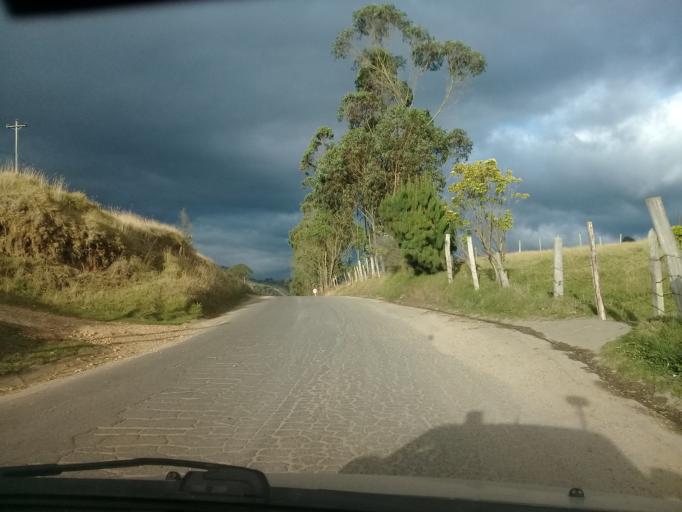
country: CO
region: Cundinamarca
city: Villapinzon
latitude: 5.2147
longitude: -73.6249
